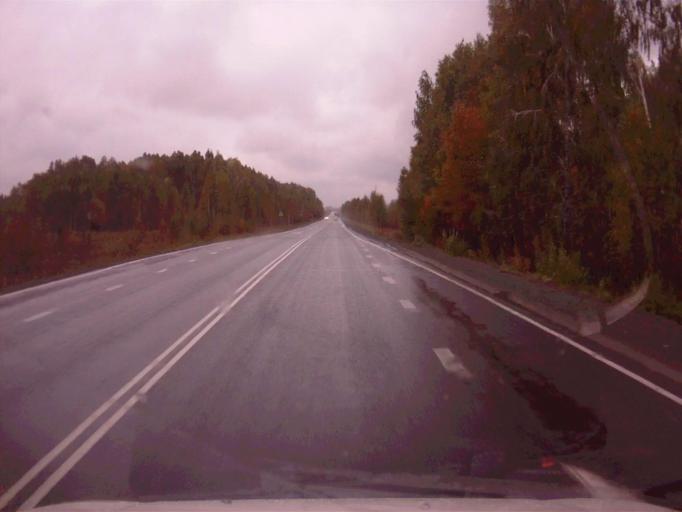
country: RU
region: Chelyabinsk
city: Novogornyy
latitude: 55.4893
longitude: 60.6865
